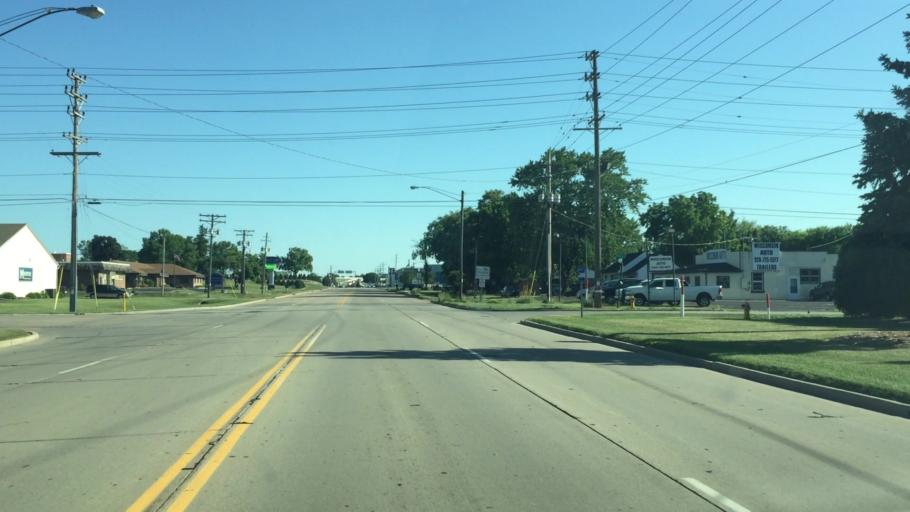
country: US
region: Wisconsin
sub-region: Winnebago County
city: Neenah
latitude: 44.1923
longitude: -88.4851
